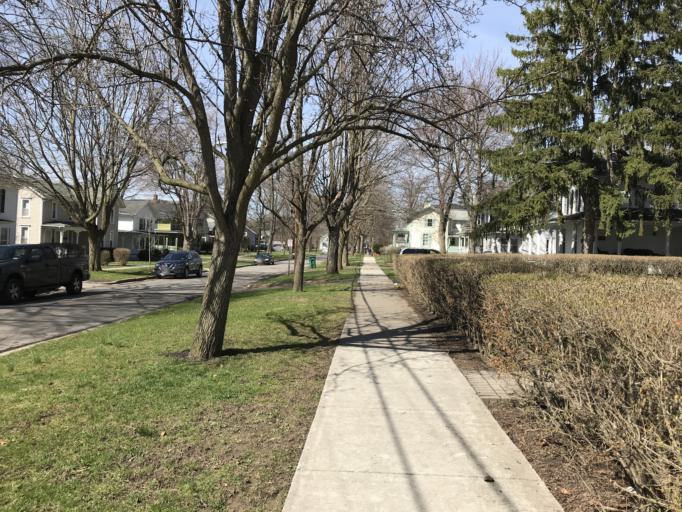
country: US
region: New York
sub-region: Livingston County
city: Geneseo
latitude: 42.7980
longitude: -77.8140
